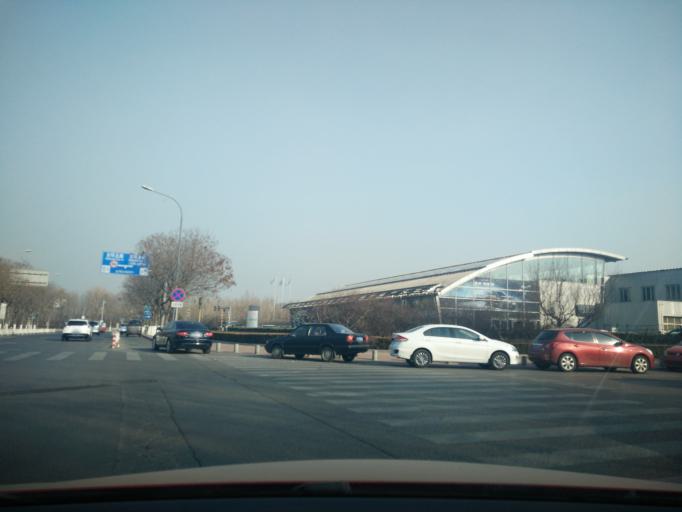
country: CN
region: Beijing
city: Jiugong
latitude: 39.8096
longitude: 116.5050
